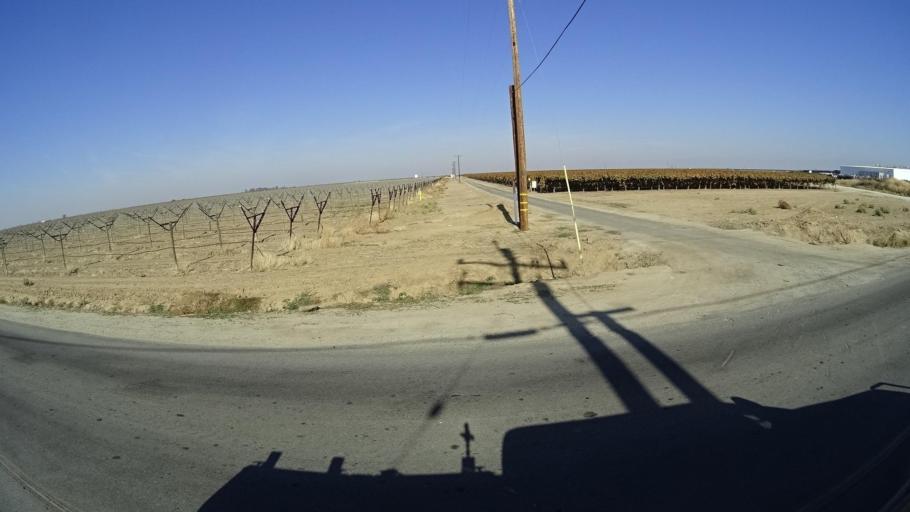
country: US
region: California
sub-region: Kern County
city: McFarland
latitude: 35.7181
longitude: -119.1608
